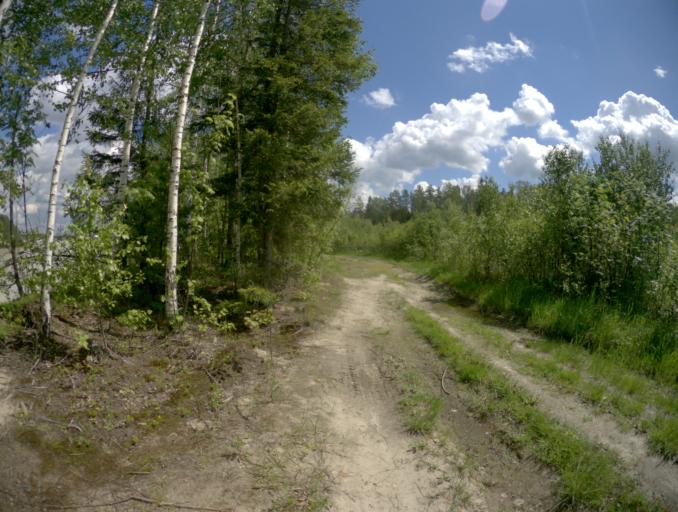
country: RU
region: Vladimir
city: Velikodvorskiy
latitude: 55.2260
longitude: 40.6335
